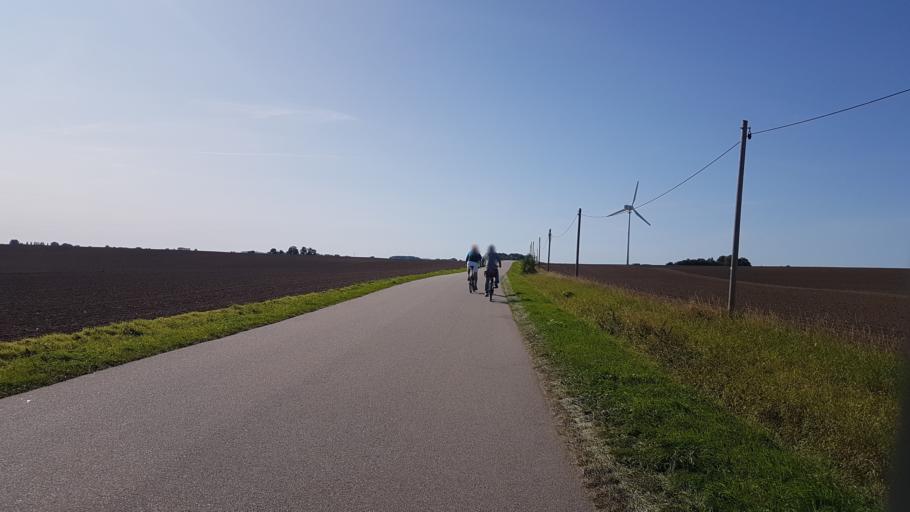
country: DE
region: Mecklenburg-Vorpommern
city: Altenkirchen
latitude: 54.6597
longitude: 13.3337
